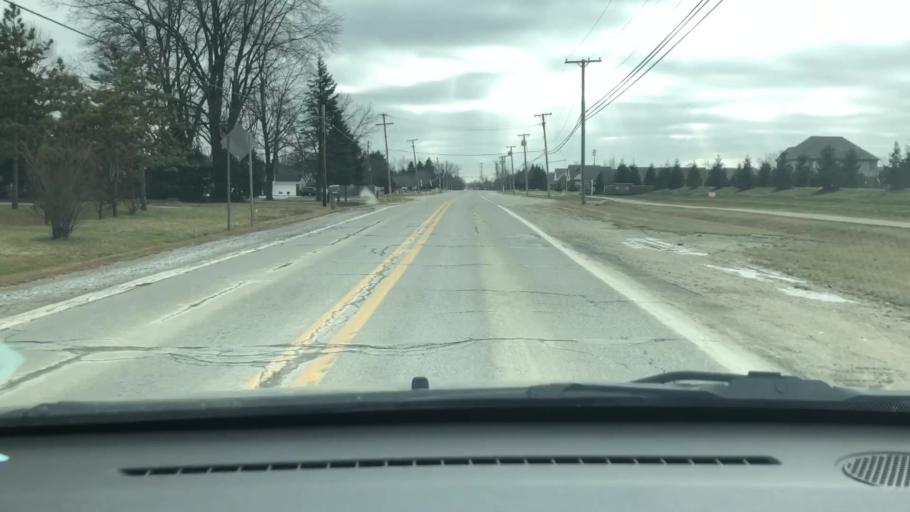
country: US
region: Michigan
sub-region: Macomb County
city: Romeo
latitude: 42.7417
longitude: -83.0367
